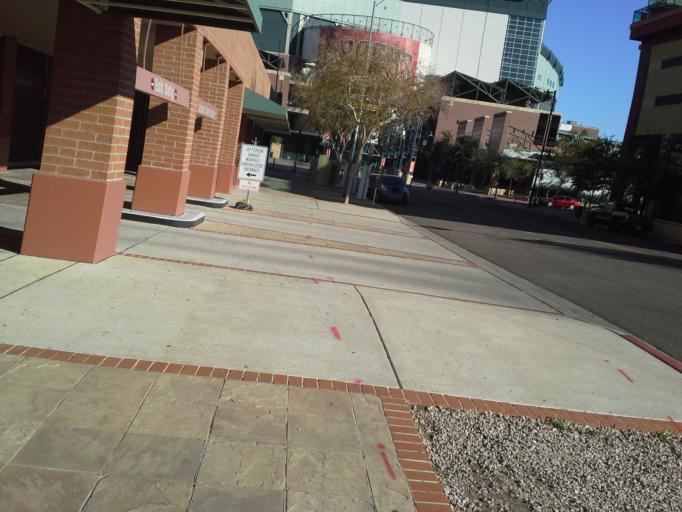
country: US
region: Arizona
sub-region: Maricopa County
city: Phoenix
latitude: 33.4451
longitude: -112.0695
